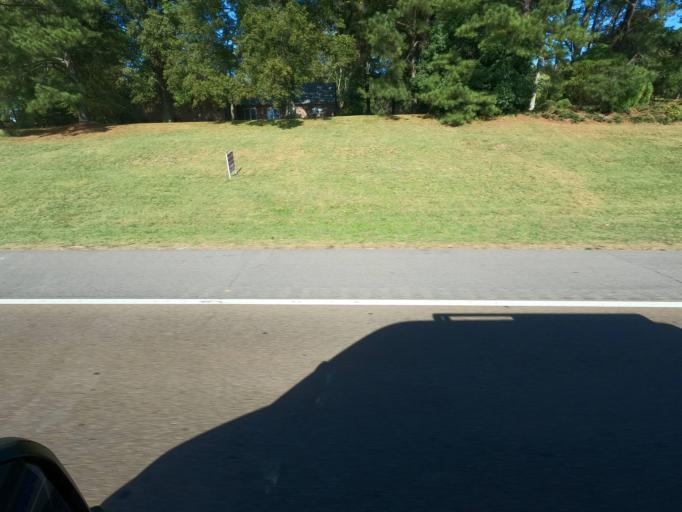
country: US
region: Tennessee
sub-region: Tipton County
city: Munford
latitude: 35.4171
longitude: -89.8256
